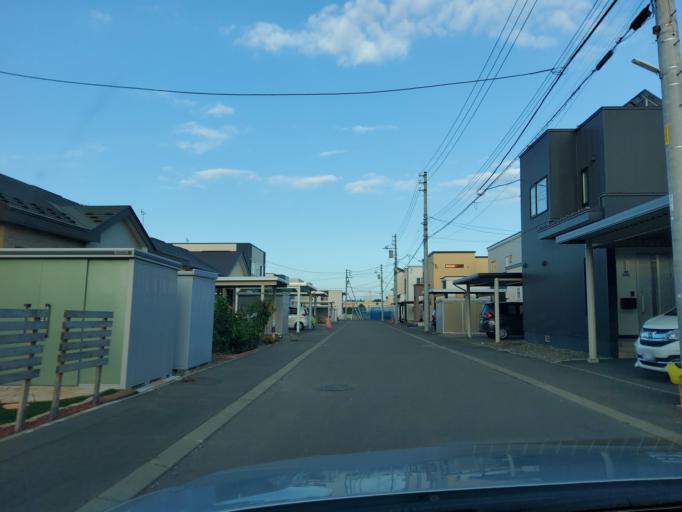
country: JP
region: Hokkaido
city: Obihiro
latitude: 42.9349
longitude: 143.1810
